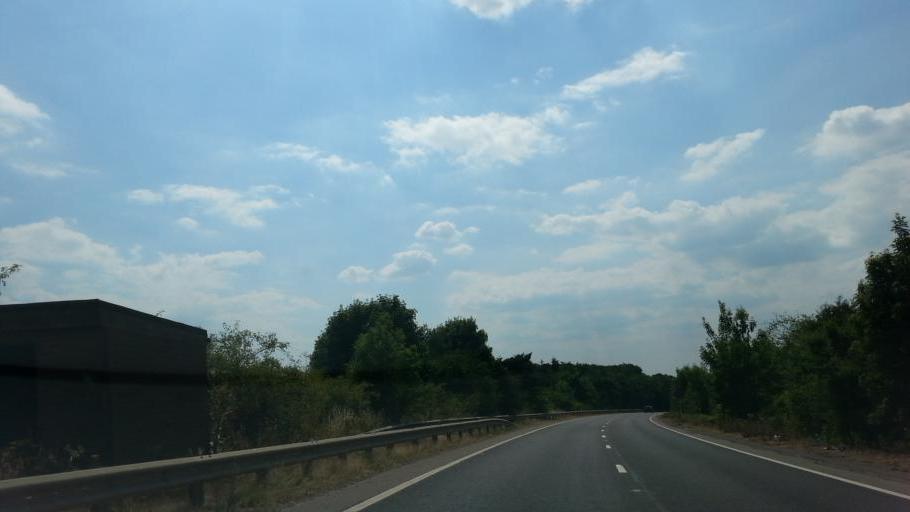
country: GB
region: England
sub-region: Suffolk
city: Newmarket
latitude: 52.2721
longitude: 0.4491
